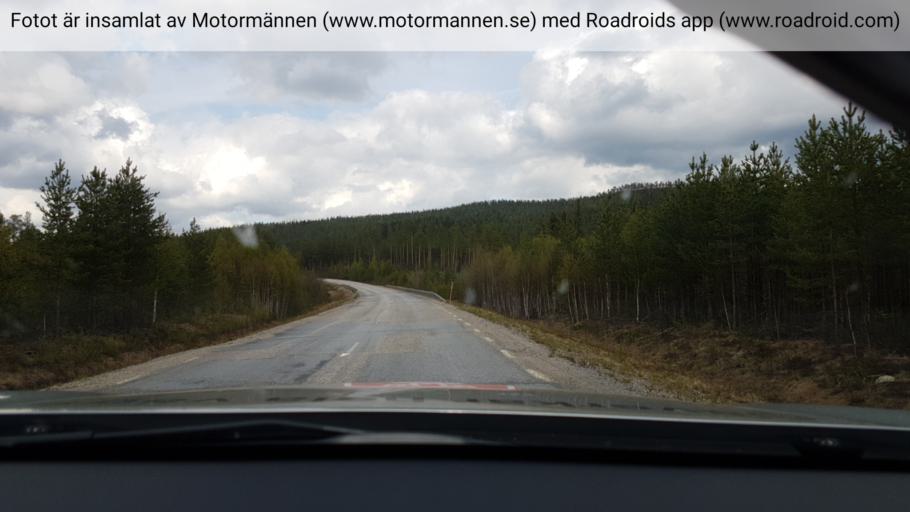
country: SE
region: Vaesternorrland
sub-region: OErnskoeldsviks Kommun
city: Bredbyn
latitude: 63.9286
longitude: 18.4823
